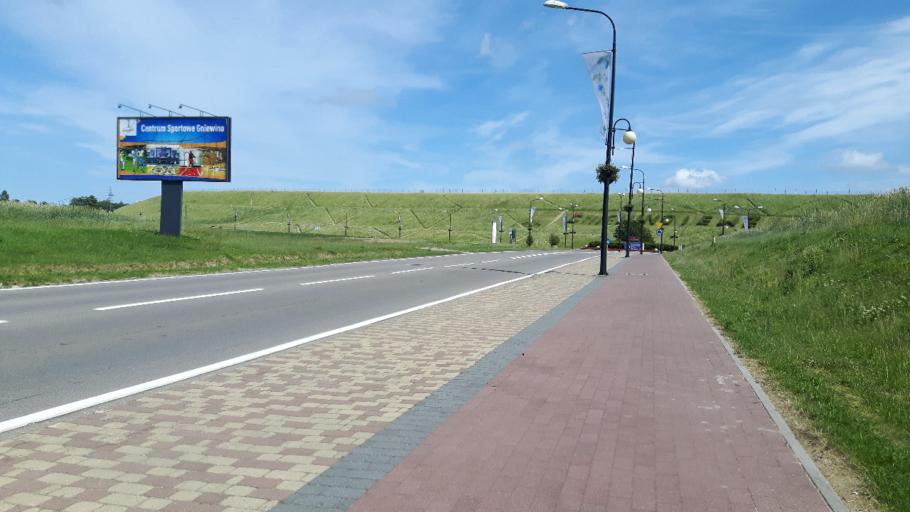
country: PL
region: Pomeranian Voivodeship
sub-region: Powiat wejherowski
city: Gniewino
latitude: 54.7146
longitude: 18.0465
